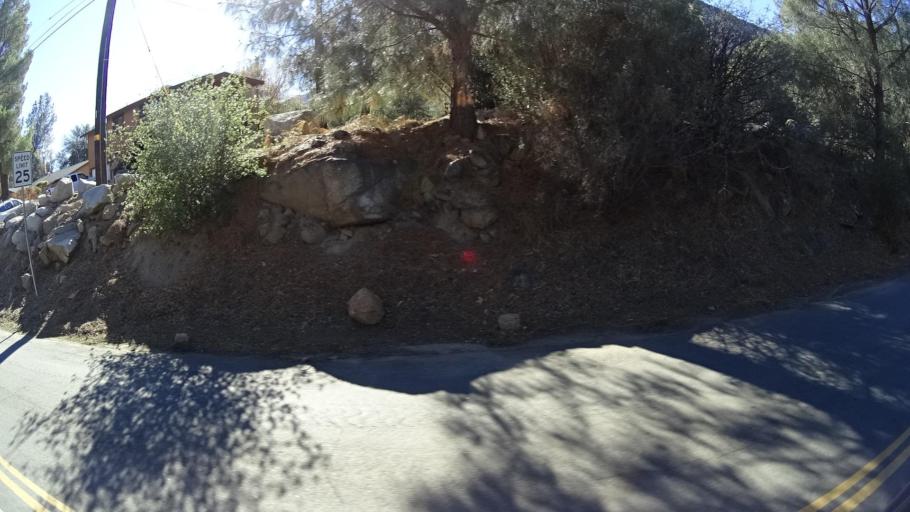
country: US
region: California
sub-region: Kern County
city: Kernville
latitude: 35.7695
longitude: -118.4362
